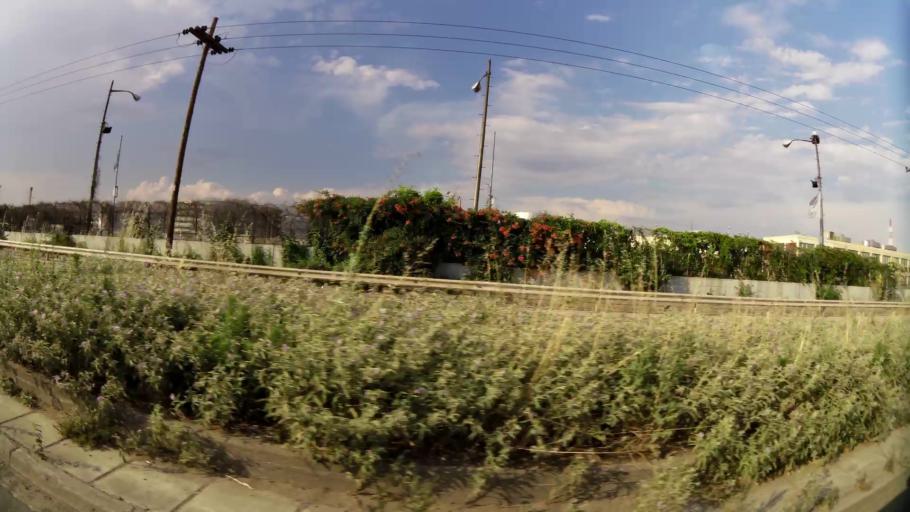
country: GR
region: Central Macedonia
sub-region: Nomos Thessalonikis
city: Diavata
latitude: 40.6757
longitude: 22.8756
